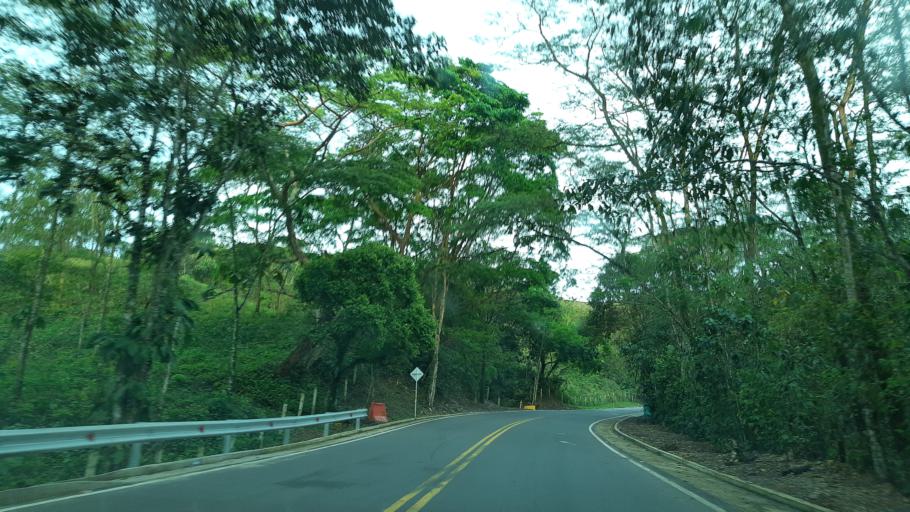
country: CO
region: Casanare
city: Sabanalarga
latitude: 4.7595
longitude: -73.0240
